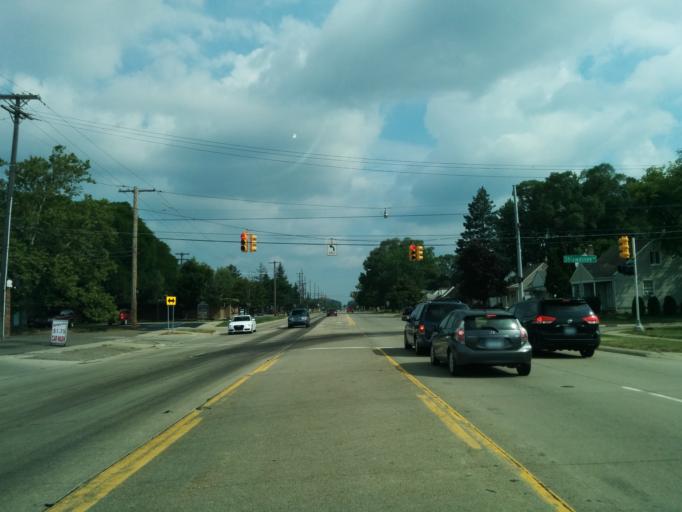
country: US
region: Michigan
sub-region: Oakland County
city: Farmington
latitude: 42.4593
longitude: -83.3566
